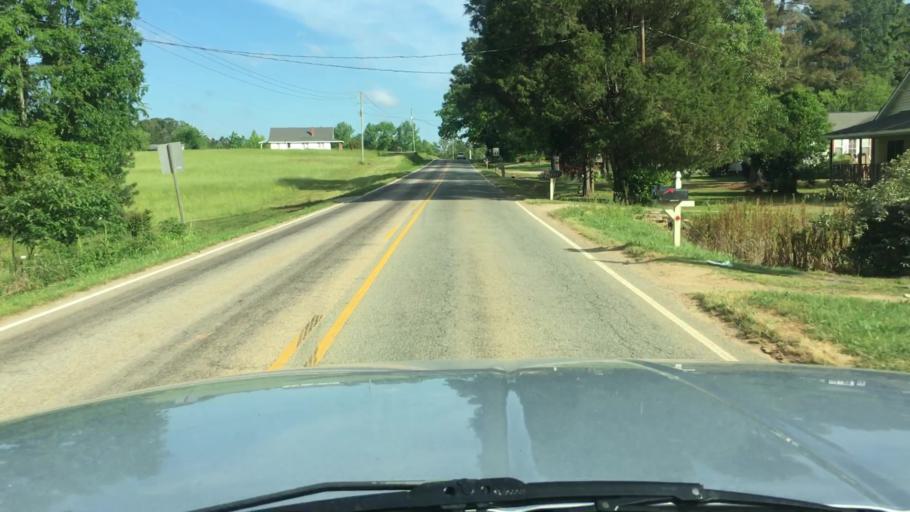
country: US
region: North Carolina
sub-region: Johnston County
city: Wilsons Mills
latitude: 35.6391
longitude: -78.3371
